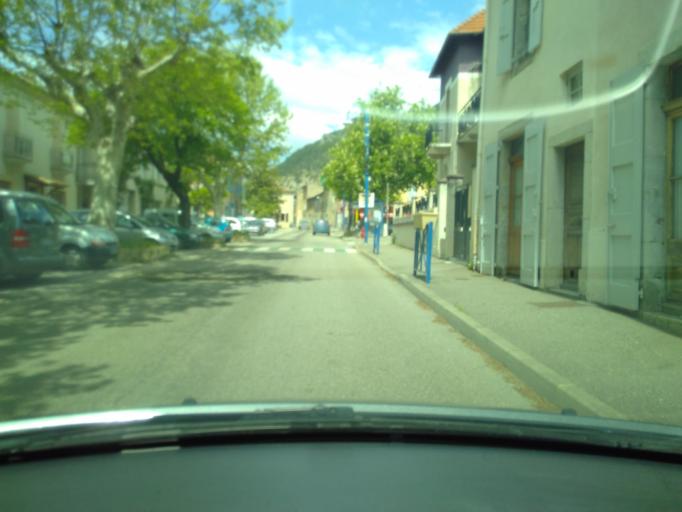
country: FR
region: Rhone-Alpes
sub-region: Departement de la Drome
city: Die
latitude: 44.6132
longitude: 5.4531
